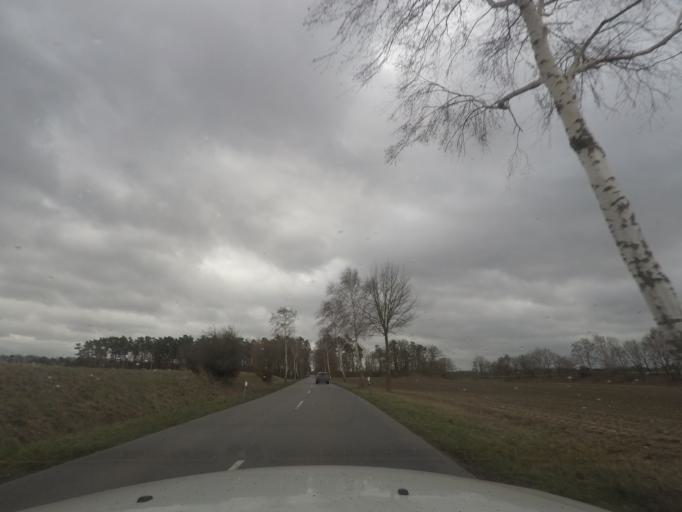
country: DE
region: Lower Saxony
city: Emmendorf
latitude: 53.0357
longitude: 10.6045
